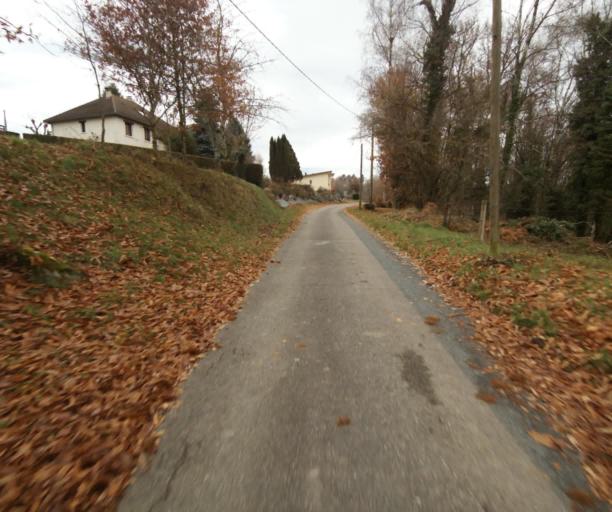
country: FR
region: Limousin
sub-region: Departement de la Correze
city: Sainte-Fortunade
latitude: 45.2272
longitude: 1.7579
